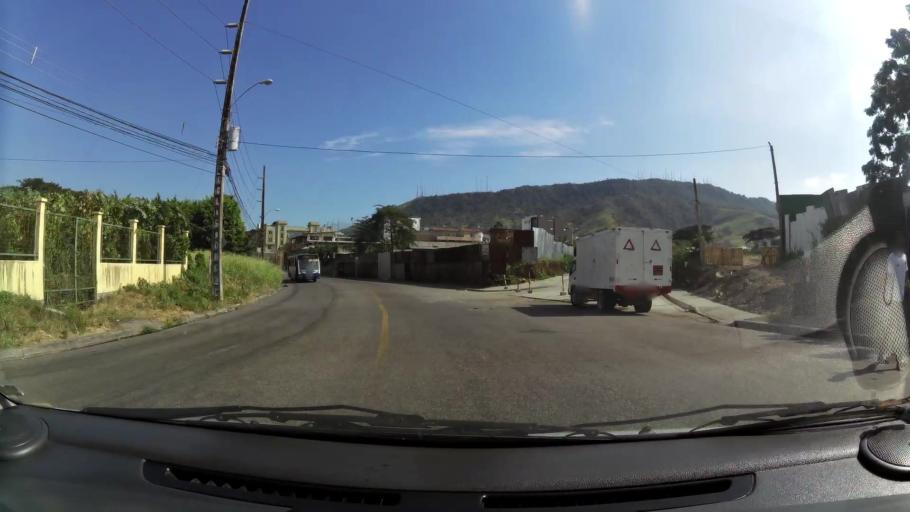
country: EC
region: Guayas
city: Guayaquil
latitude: -2.1592
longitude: -79.9398
